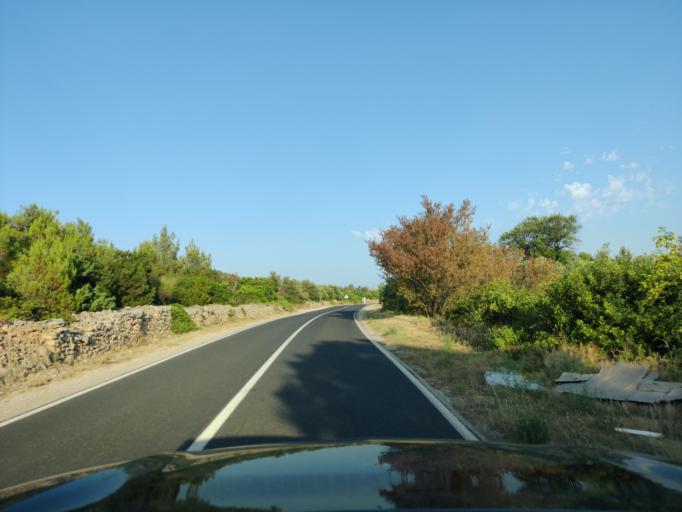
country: HR
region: Sibensko-Kniniska
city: Tribunj
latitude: 43.7661
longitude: 15.7345
